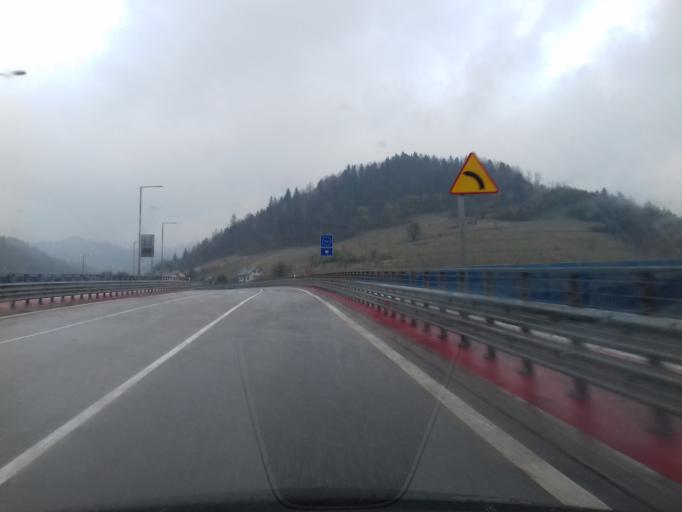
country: PL
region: Lesser Poland Voivodeship
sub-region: Powiat nowosadecki
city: Piwniczna-Zdroj
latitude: 49.4174
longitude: 20.7237
